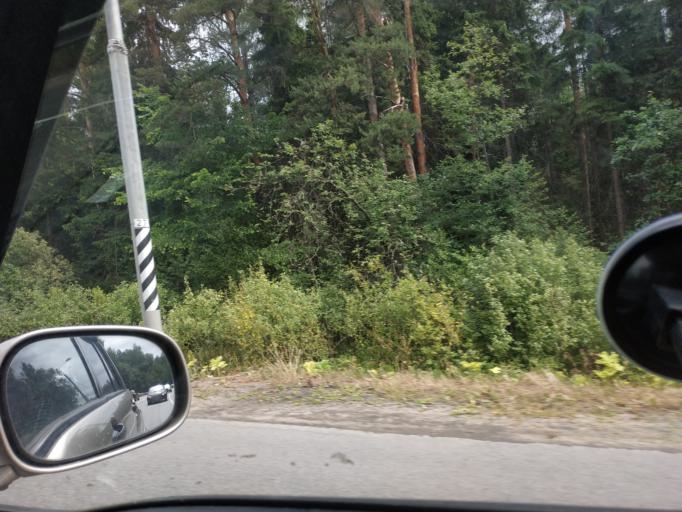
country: RU
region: Moskovskaya
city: Krasnoarmeysk
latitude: 56.0166
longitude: 38.1581
